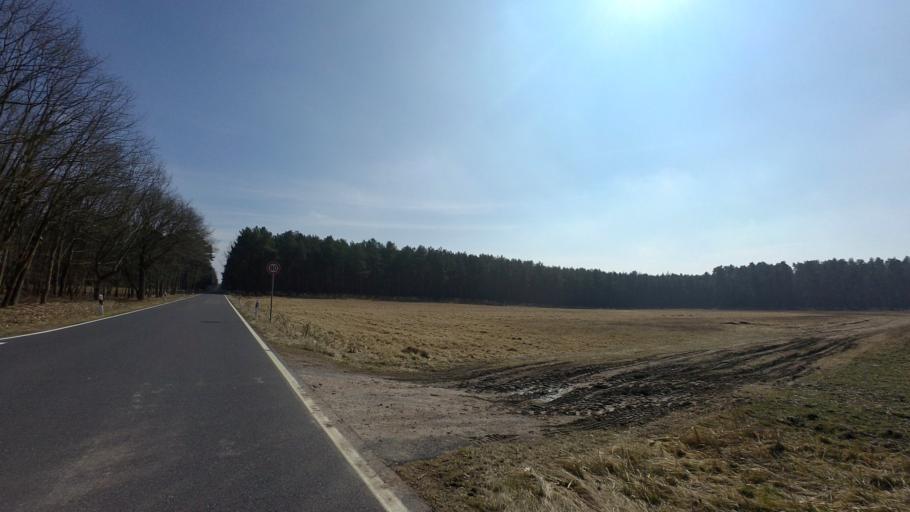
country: DE
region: Saxony-Anhalt
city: Nudersdorf
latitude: 52.0197
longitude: 12.5558
